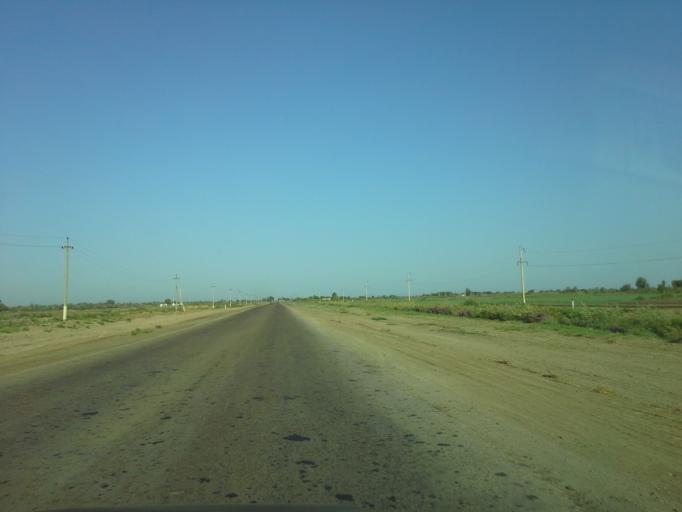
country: UZ
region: Karakalpakstan
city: Khujayli
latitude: 42.2239
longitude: 59.4816
